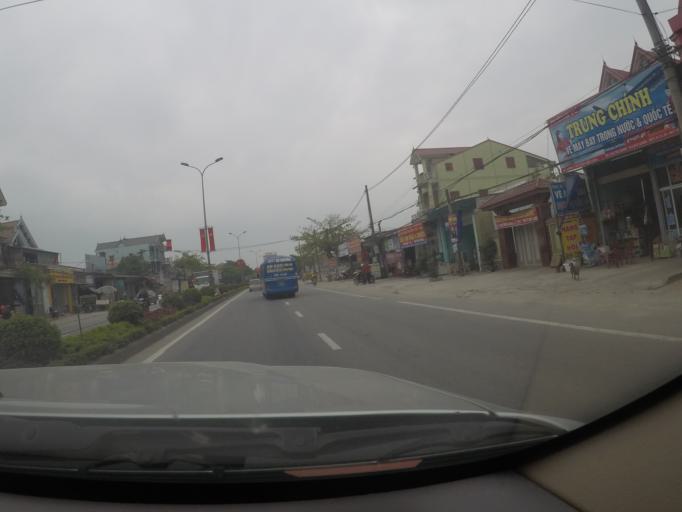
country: VN
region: Nghe An
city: Dien Chau
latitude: 18.9744
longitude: 105.6009
